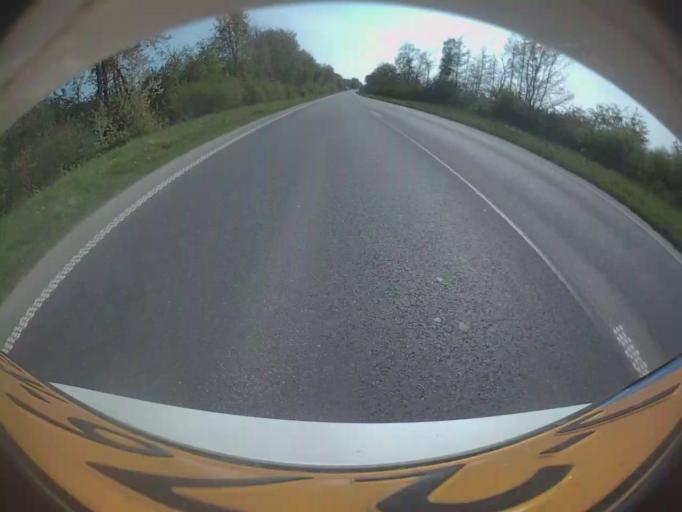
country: BE
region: Wallonia
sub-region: Province de Namur
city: Ciney
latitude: 50.2974
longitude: 5.1181
